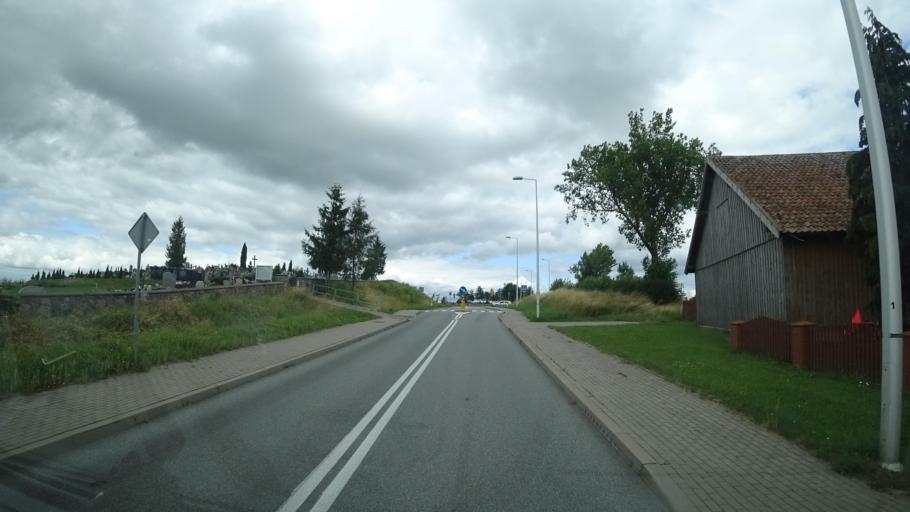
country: PL
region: Warmian-Masurian Voivodeship
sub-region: Powiat goldapski
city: Goldap
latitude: 54.2277
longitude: 22.2440
